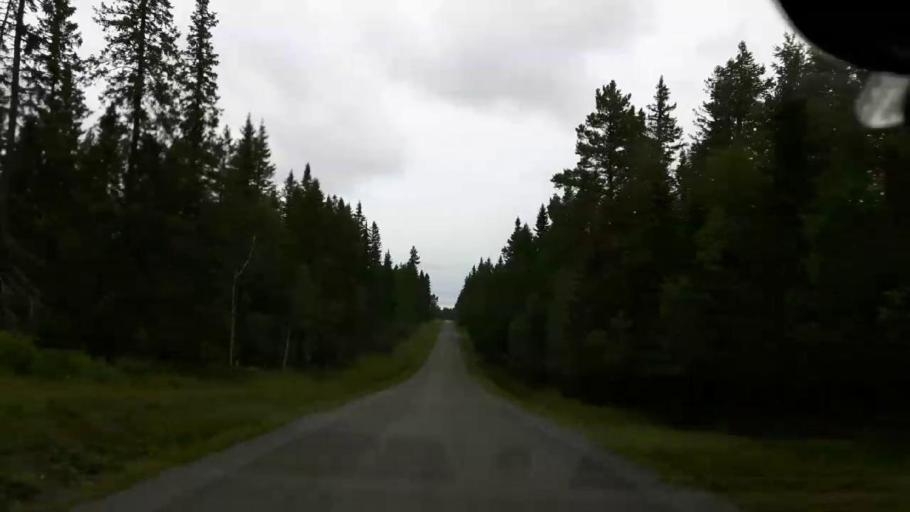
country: SE
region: Jaemtland
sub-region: OEstersunds Kommun
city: Ostersund
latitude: 63.0983
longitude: 14.5455
